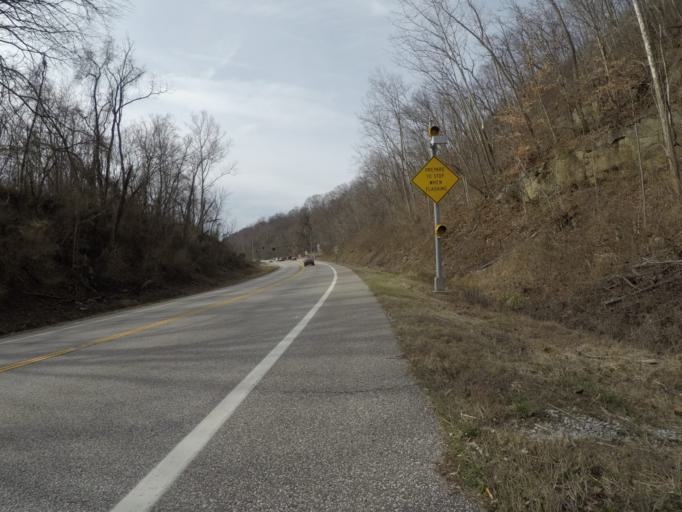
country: US
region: West Virginia
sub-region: Cabell County
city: Huntington
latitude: 38.4435
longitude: -82.4036
